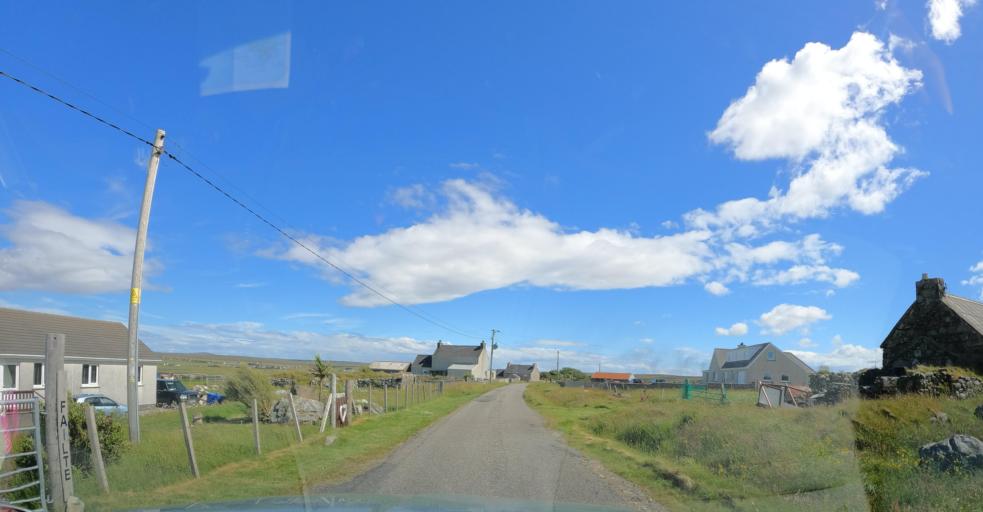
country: GB
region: Scotland
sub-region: Eilean Siar
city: Isle of Lewis
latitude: 58.3547
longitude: -6.5492
